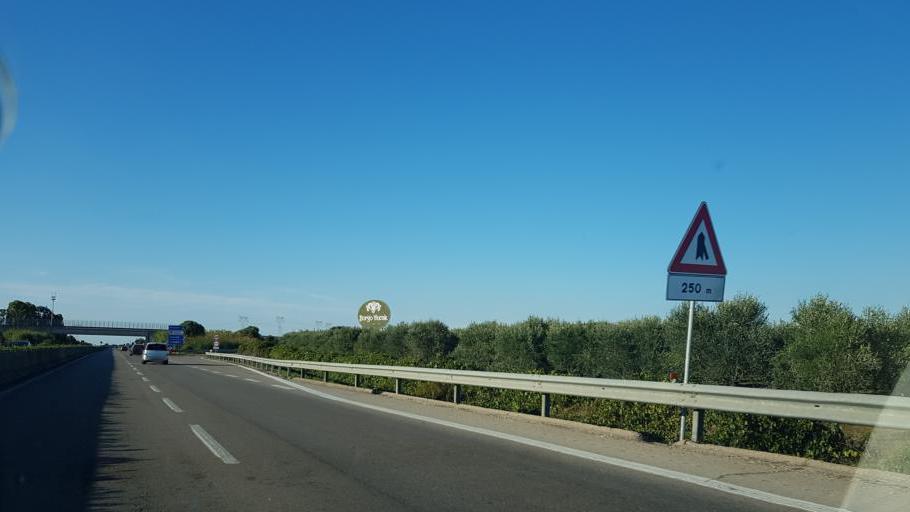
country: IT
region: Apulia
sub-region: Provincia di Brindisi
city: Tuturano
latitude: 40.5514
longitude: 17.9964
